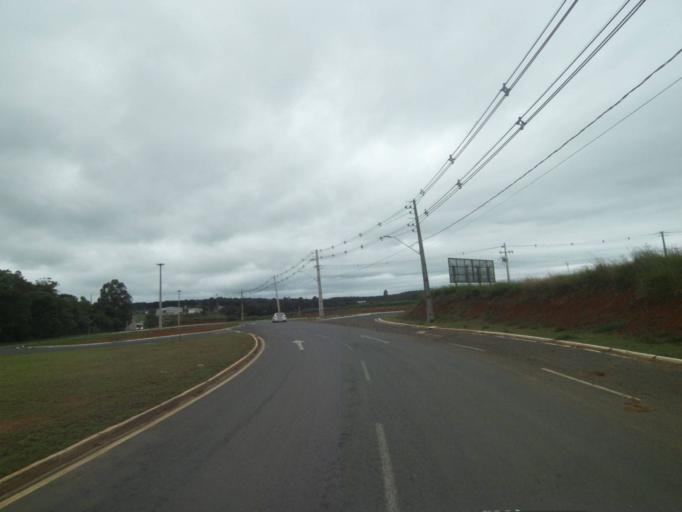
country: BR
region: Parana
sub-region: Telemaco Borba
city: Telemaco Borba
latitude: -24.3850
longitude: -50.6759
